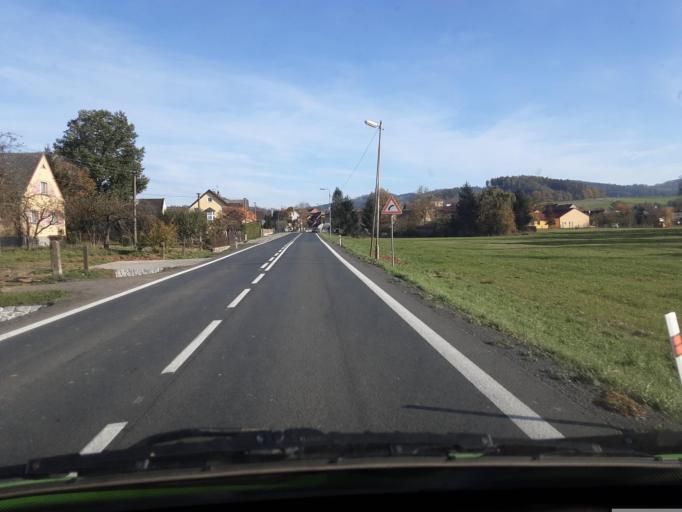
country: CZ
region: Plzensky
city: Klatovy
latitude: 49.3624
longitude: 13.3500
